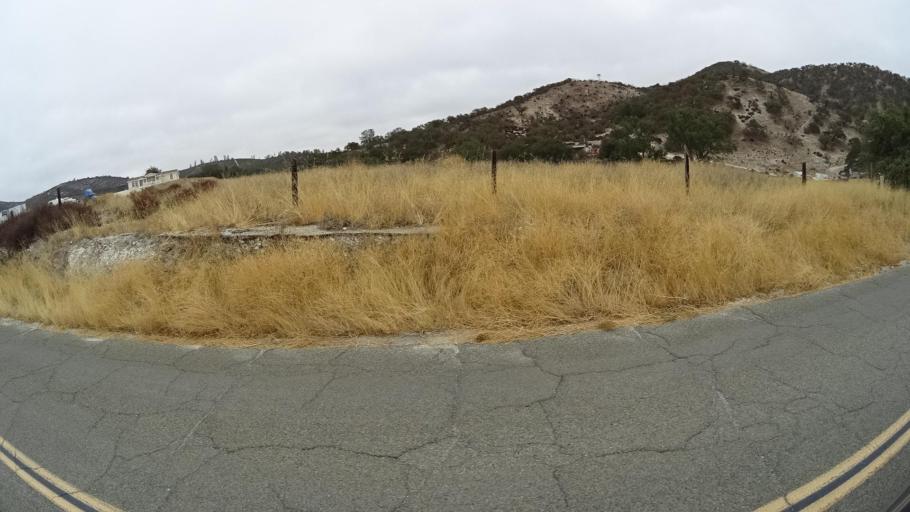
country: US
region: California
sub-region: San Luis Obispo County
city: Lake Nacimiento
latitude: 35.9023
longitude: -120.9848
